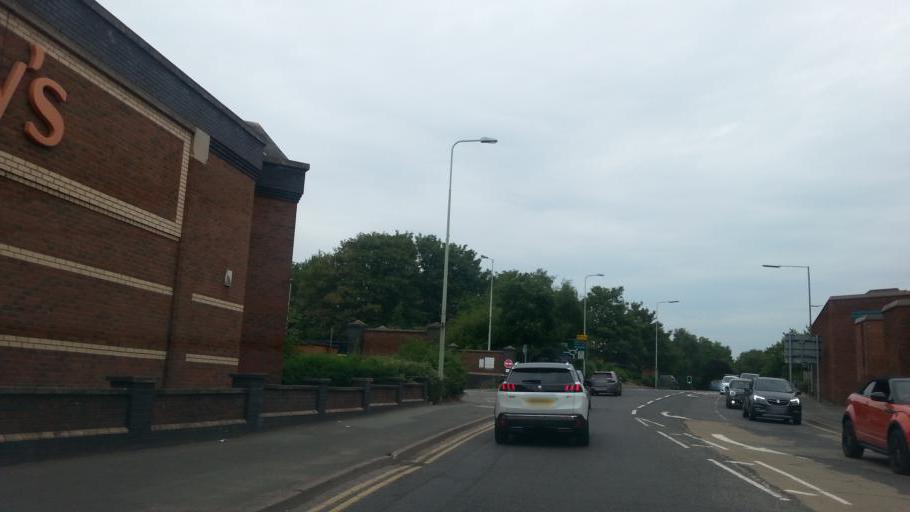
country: GB
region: England
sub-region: Staffordshire
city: Stafford
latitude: 52.8083
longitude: -2.1209
